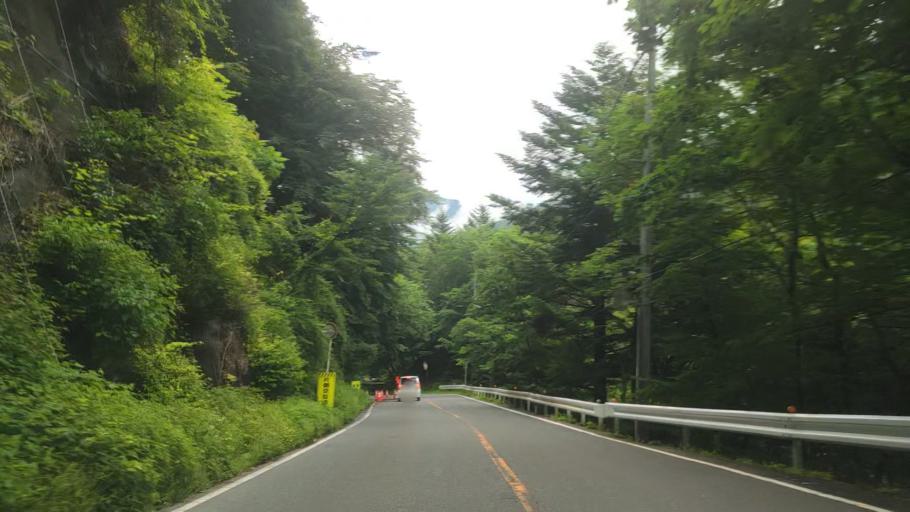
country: JP
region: Yamanashi
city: Enzan
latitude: 35.9139
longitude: 138.8231
